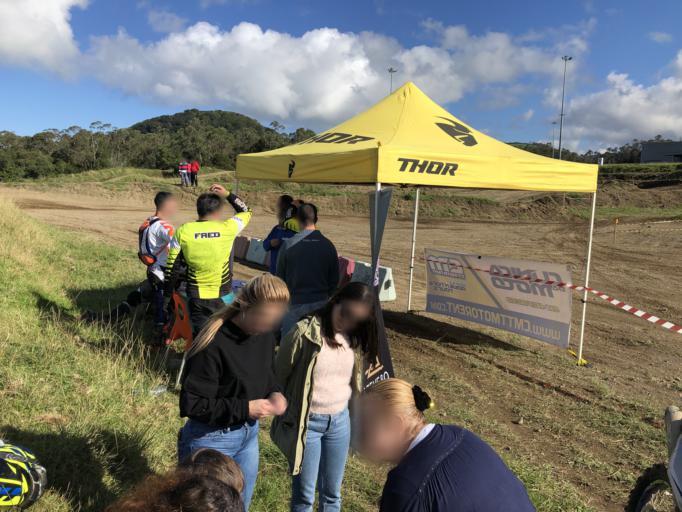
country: PT
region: Azores
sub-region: Ribeira Grande
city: Rabo de Peixe
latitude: 37.7792
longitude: -25.5691
